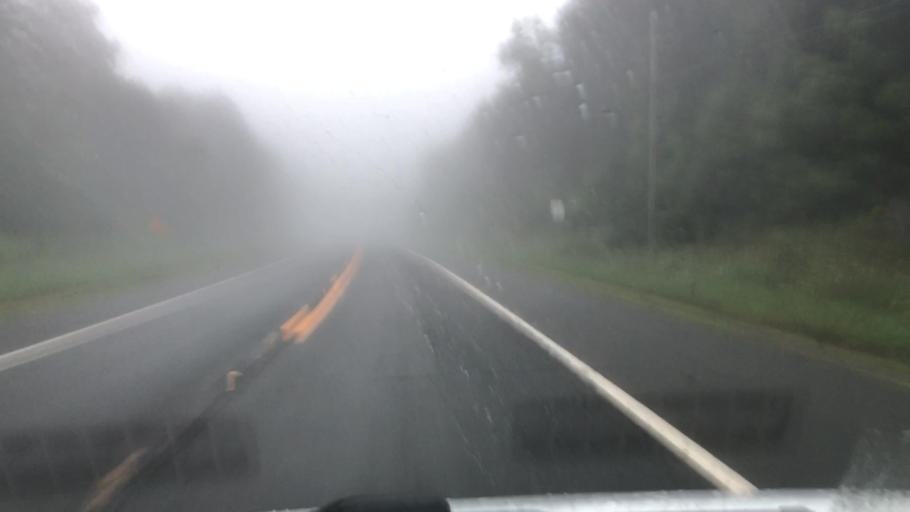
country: US
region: Massachusetts
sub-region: Berkshire County
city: Hinsdale
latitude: 42.5079
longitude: -73.0425
